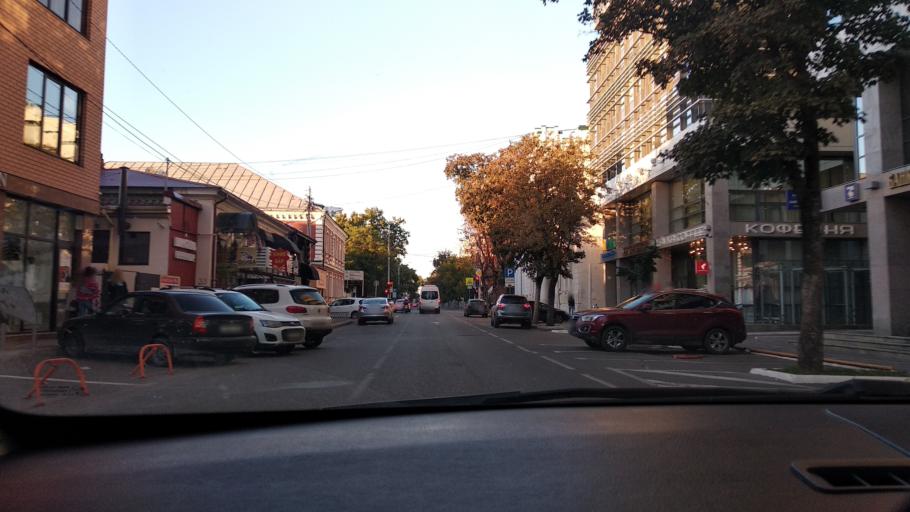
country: RU
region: Krasnodarskiy
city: Krasnodar
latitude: 45.0227
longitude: 38.9718
